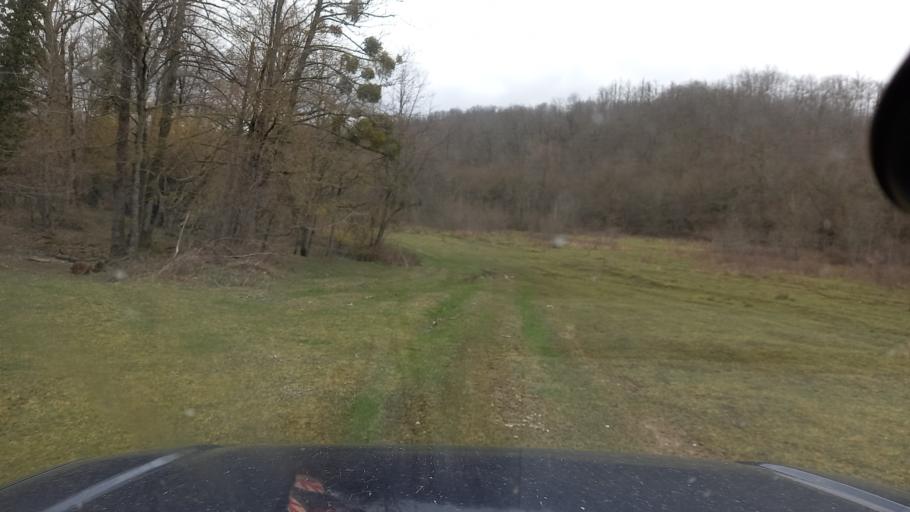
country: RU
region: Krasnodarskiy
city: Pshada
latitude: 44.4844
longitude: 38.4002
